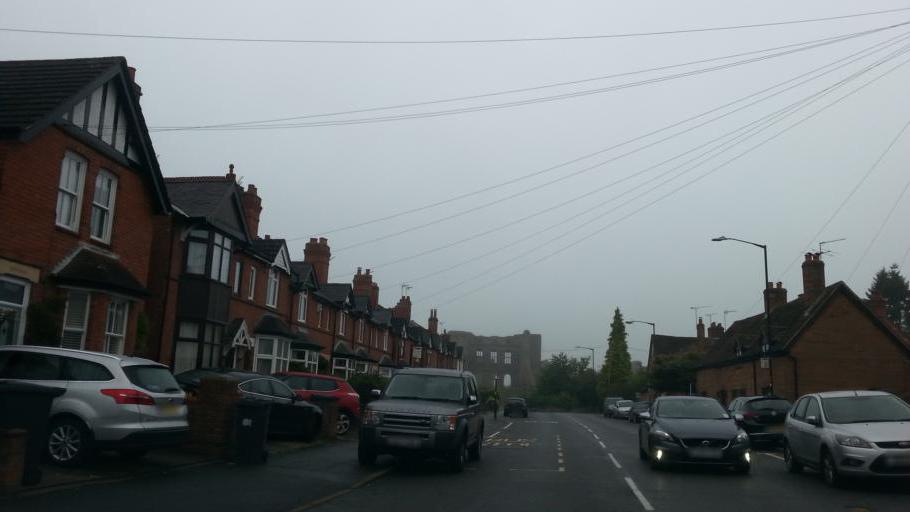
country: GB
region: England
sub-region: Warwickshire
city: Kenilworth
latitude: 52.3502
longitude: -1.5924
